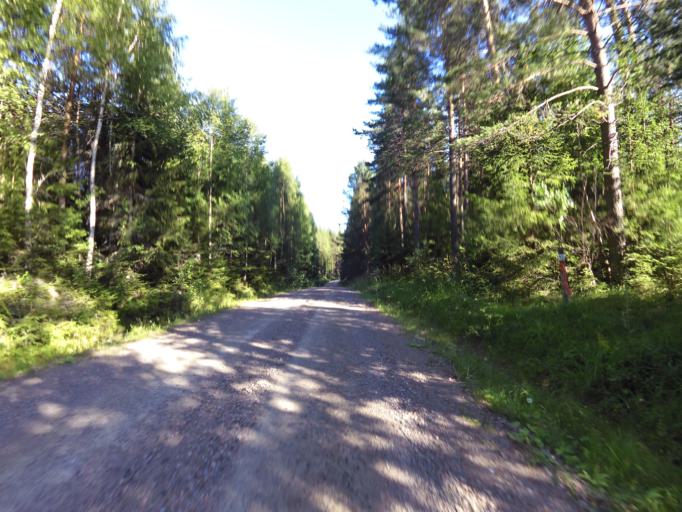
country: SE
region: Gaevleborg
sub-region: Hofors Kommun
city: Hofors
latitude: 60.6446
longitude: 16.2770
